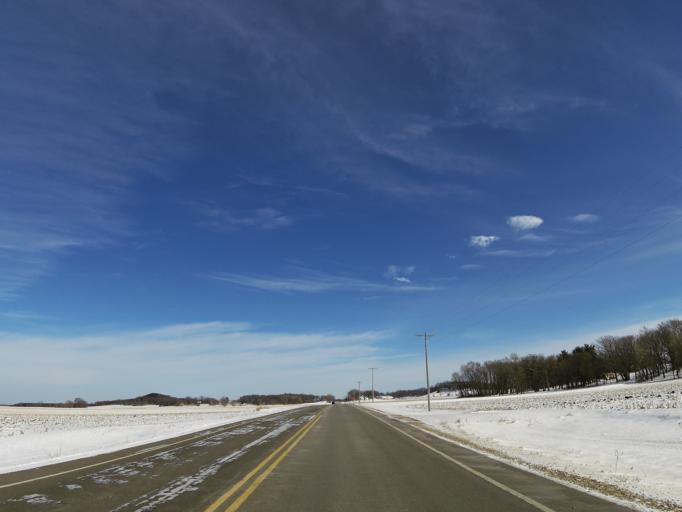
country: US
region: Wisconsin
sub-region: Pierce County
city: Prescott
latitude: 44.7959
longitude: -92.7595
